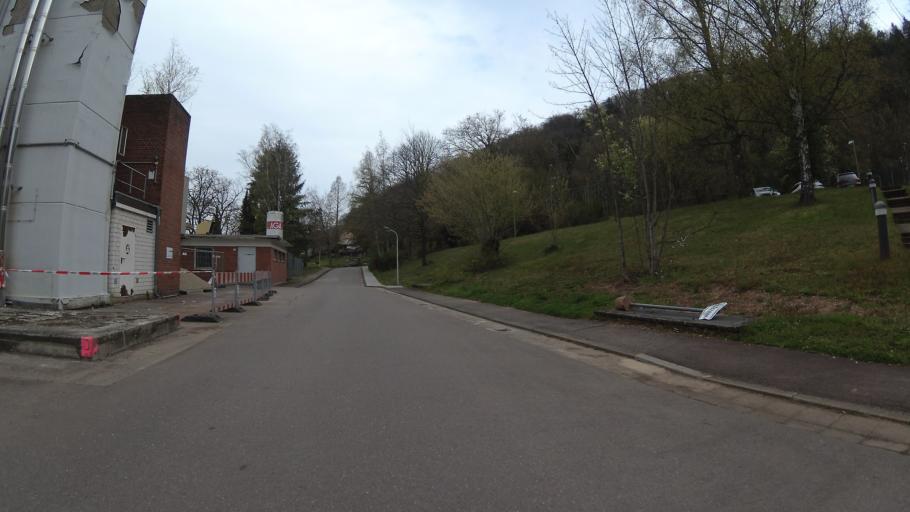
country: DE
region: Saarland
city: Merzig
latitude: 49.4579
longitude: 6.6336
